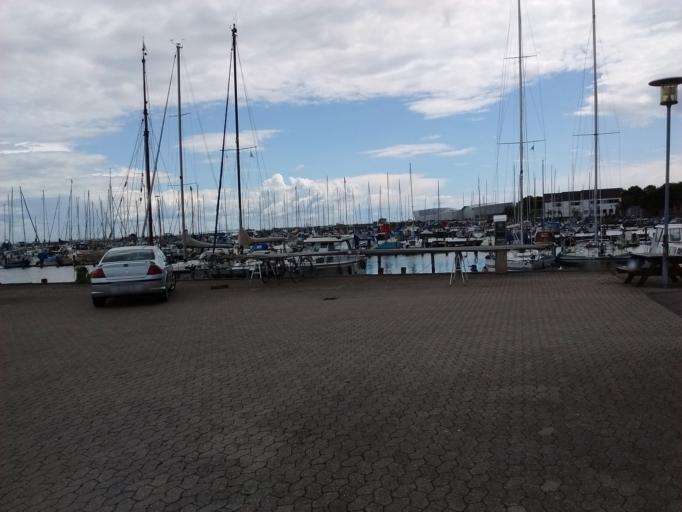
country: DK
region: Capital Region
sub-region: Dragor Kommune
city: Dragor
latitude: 55.6426
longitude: 12.6508
